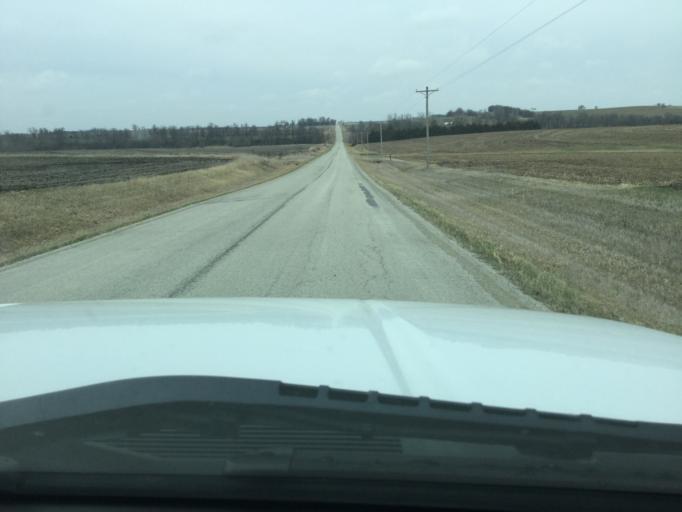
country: US
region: Kansas
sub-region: Nemaha County
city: Sabetha
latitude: 39.8968
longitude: -95.7138
